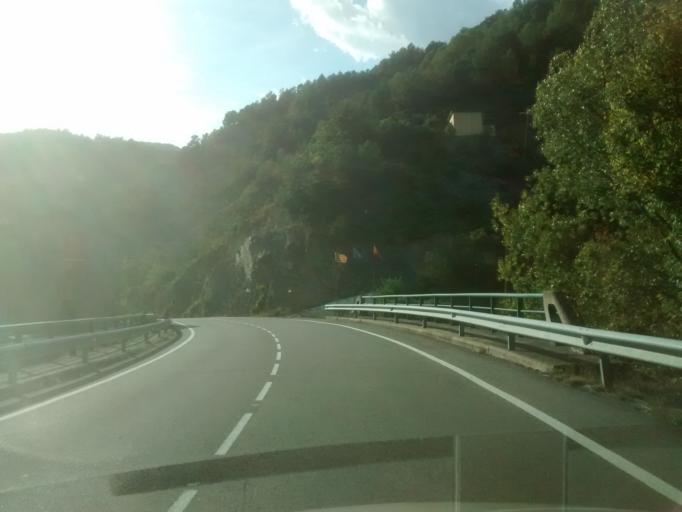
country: ES
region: Aragon
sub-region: Provincia de Huesca
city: Puertolas
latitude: 42.5478
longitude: 0.1631
